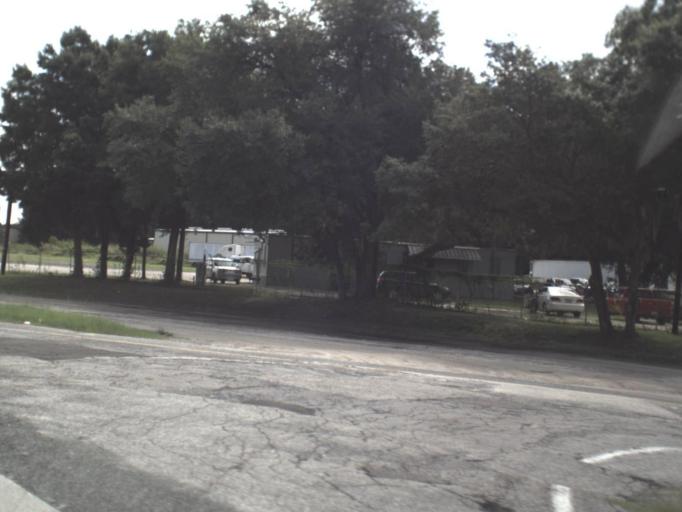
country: US
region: Florida
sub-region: Hillsborough County
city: Thonotosassa
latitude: 28.0579
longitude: -82.3116
